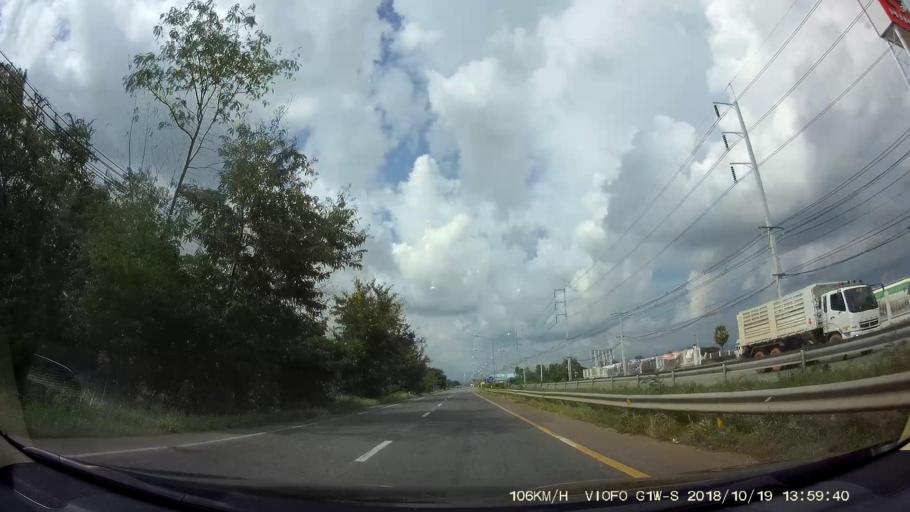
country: TH
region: Chaiyaphum
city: Chaiyaphum
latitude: 15.8131
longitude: 102.0605
